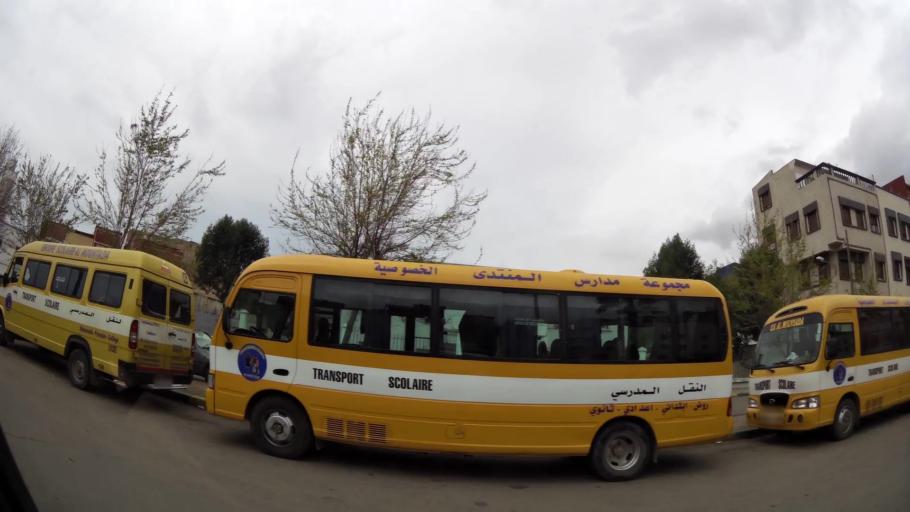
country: MA
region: Grand Casablanca
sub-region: Casablanca
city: Casablanca
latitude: 33.5564
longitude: -7.5540
